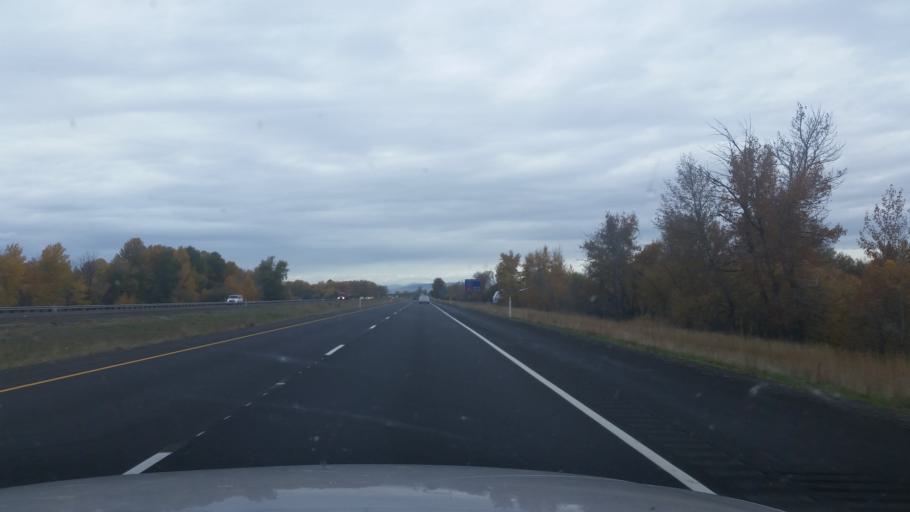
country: US
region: Washington
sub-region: Kittitas County
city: Ellensburg
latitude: 46.9962
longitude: -120.5787
